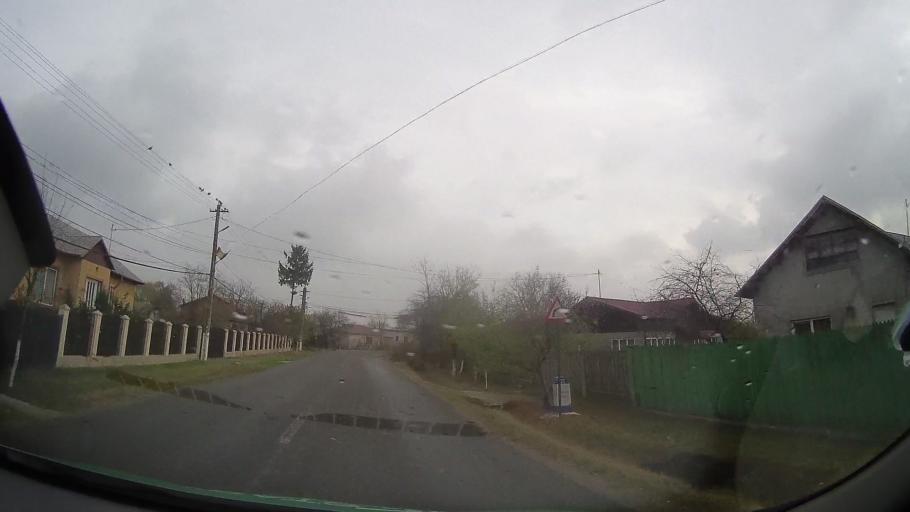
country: RO
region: Prahova
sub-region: Comuna Draganesti
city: Draganesti
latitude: 44.8286
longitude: 26.2805
